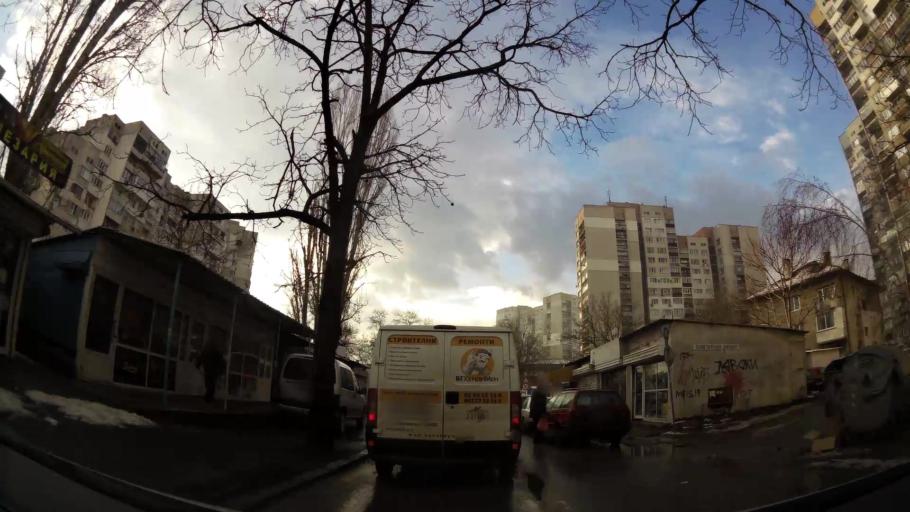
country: BG
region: Sofia-Capital
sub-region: Stolichna Obshtina
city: Sofia
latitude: 42.6973
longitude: 23.2865
